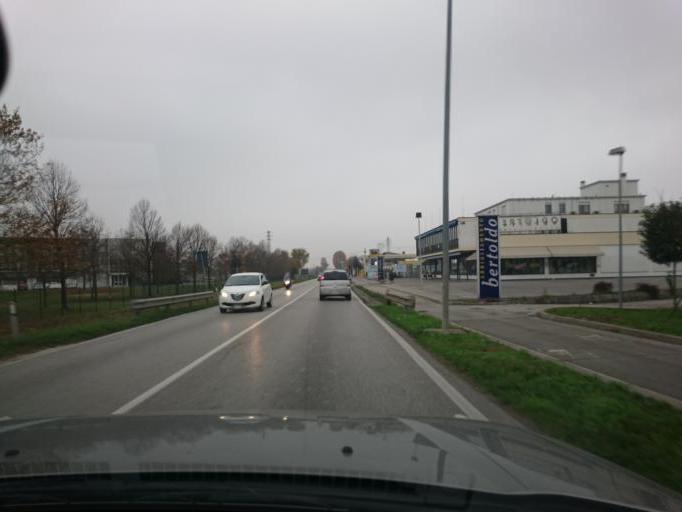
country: IT
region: Veneto
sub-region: Provincia di Padova
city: Legnaro
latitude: 45.3546
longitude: 11.9504
